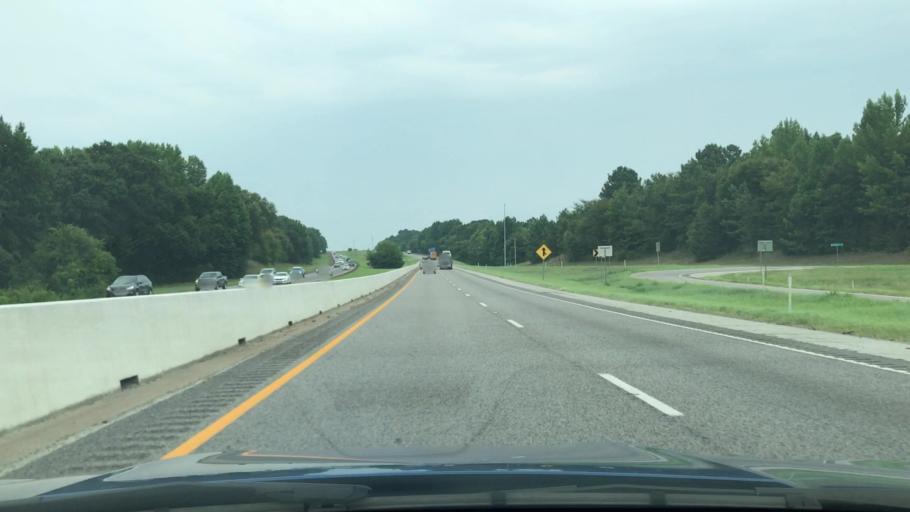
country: US
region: Texas
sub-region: Smith County
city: Tyler
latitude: 32.4576
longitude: -95.3086
